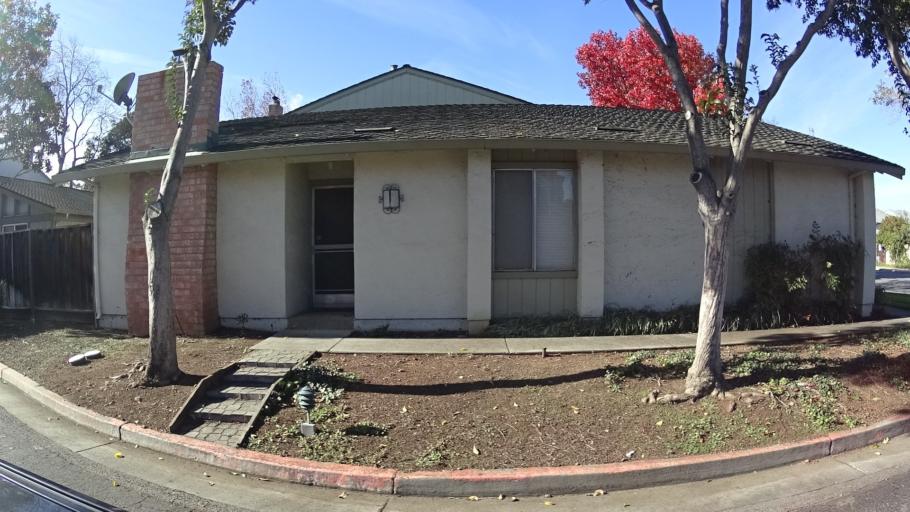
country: US
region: California
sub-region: Santa Clara County
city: Sunnyvale
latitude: 37.3508
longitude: -122.0334
